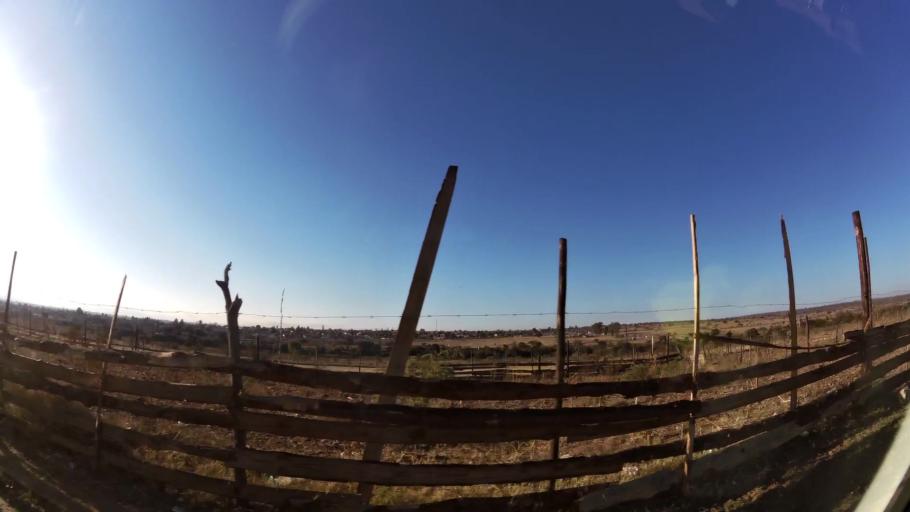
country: ZA
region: Limpopo
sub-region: Capricorn District Municipality
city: Polokwane
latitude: -23.8486
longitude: 29.3569
